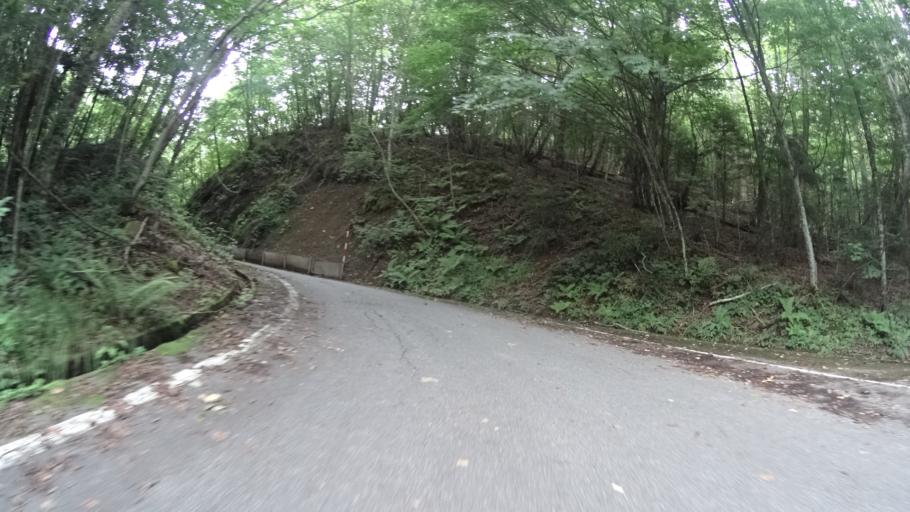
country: JP
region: Yamanashi
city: Kofu-shi
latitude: 35.8065
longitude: 138.6163
